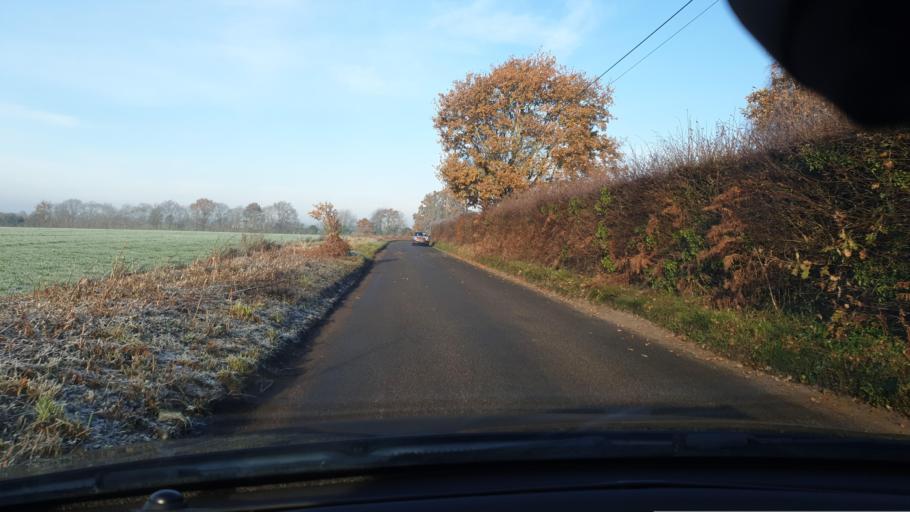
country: GB
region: England
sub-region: Essex
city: Mistley
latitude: 51.9775
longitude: 1.1139
